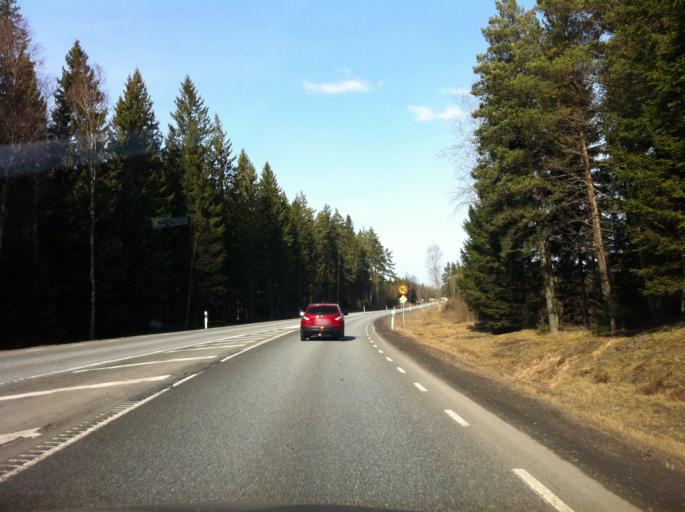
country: SE
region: Joenkoeping
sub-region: Mullsjo Kommun
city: Mullsjoe
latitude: 57.9846
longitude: 13.8277
